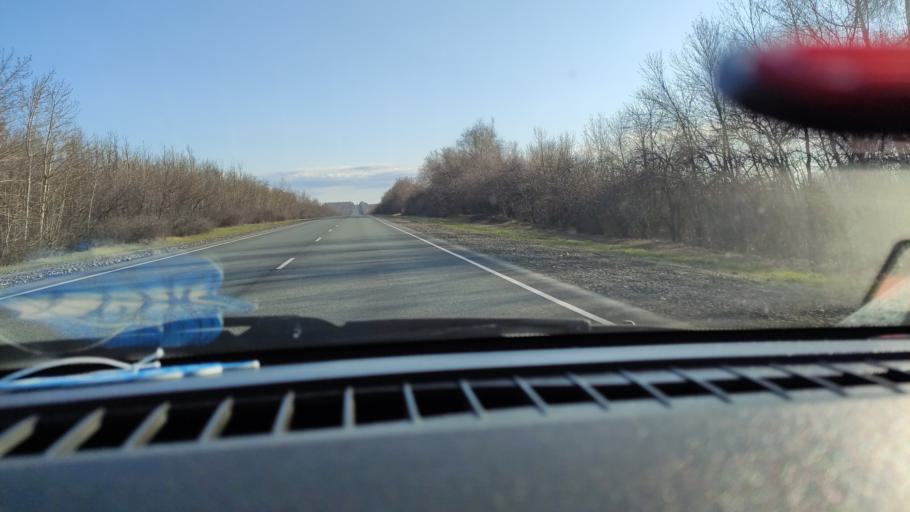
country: RU
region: Saratov
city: Khvalynsk
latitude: 52.6005
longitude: 48.1441
